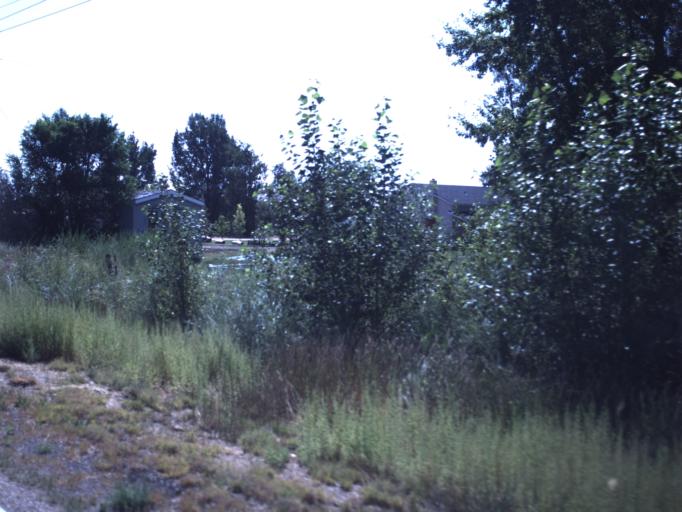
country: US
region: Utah
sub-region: Duchesne County
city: Roosevelt
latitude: 40.2581
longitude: -110.1254
